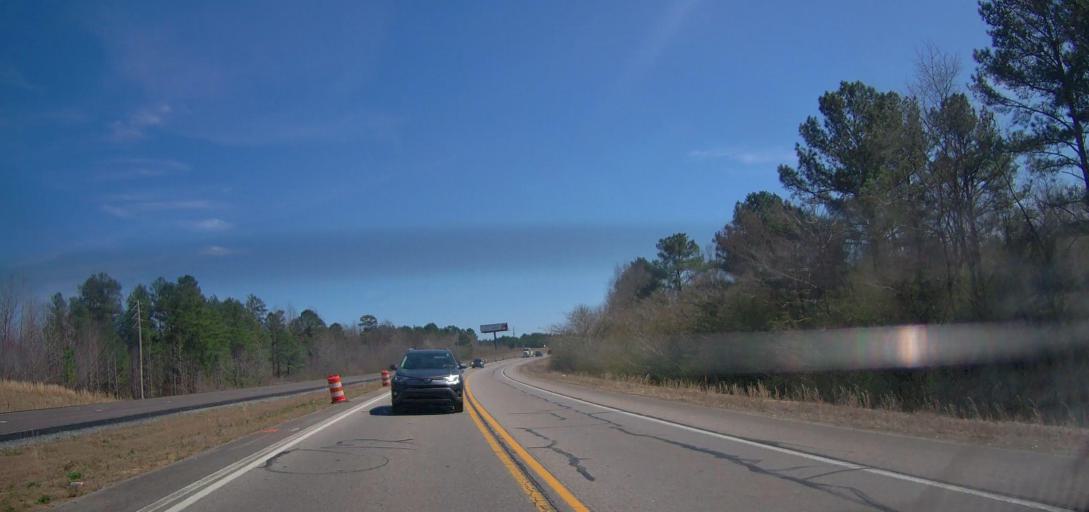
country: US
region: Alabama
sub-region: Cullman County
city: Cullman
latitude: 34.1982
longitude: -86.7925
